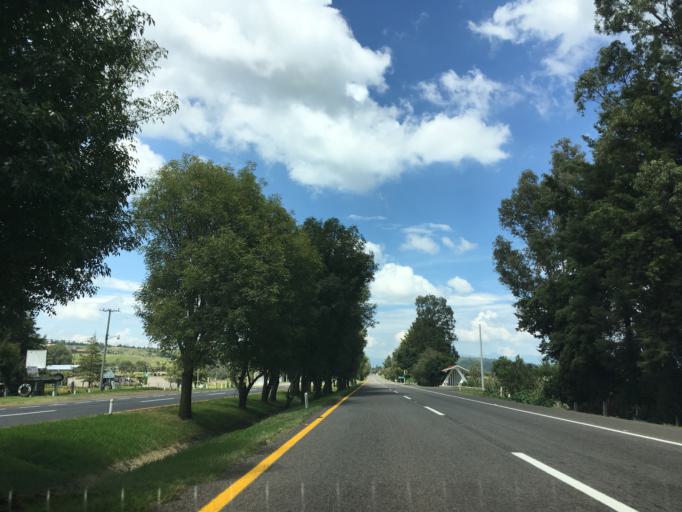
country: MX
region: Michoacan
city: Cuanajo
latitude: 19.5355
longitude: -101.5115
